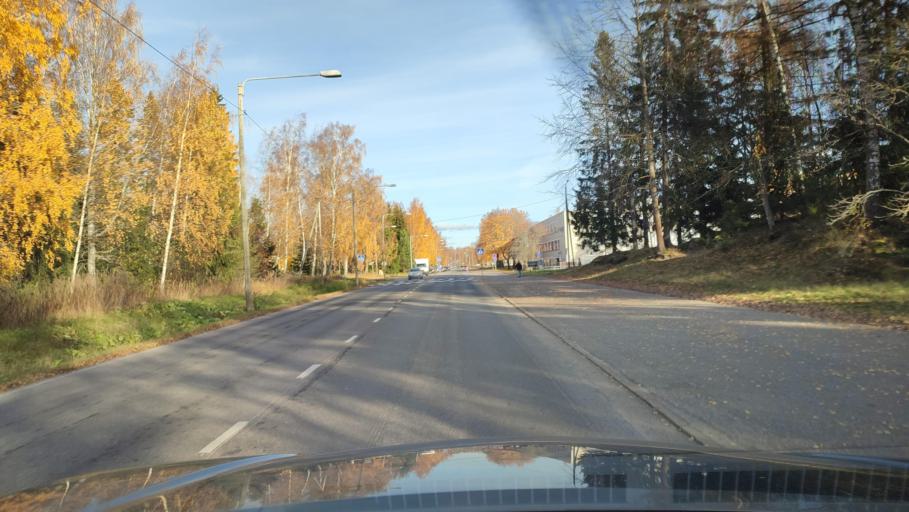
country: FI
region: Ostrobothnia
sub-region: Vaasa
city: Vaasa
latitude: 63.0841
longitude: 21.6399
